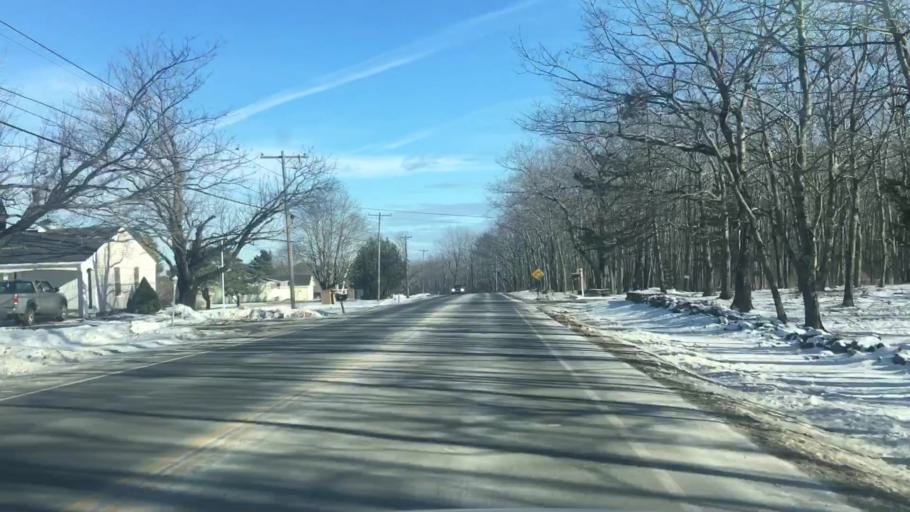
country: US
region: Maine
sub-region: Knox County
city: Rockland
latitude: 44.1297
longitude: -69.1070
